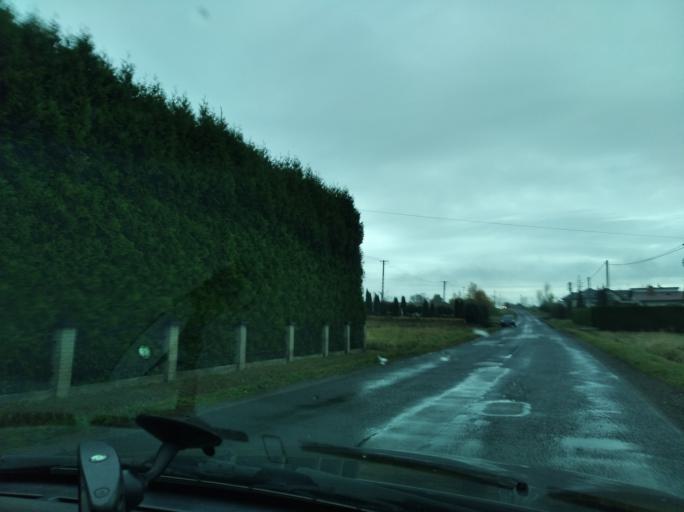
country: PL
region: Subcarpathian Voivodeship
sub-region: Powiat rzeszowski
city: Tyczyn
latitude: 49.9275
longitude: 22.0285
